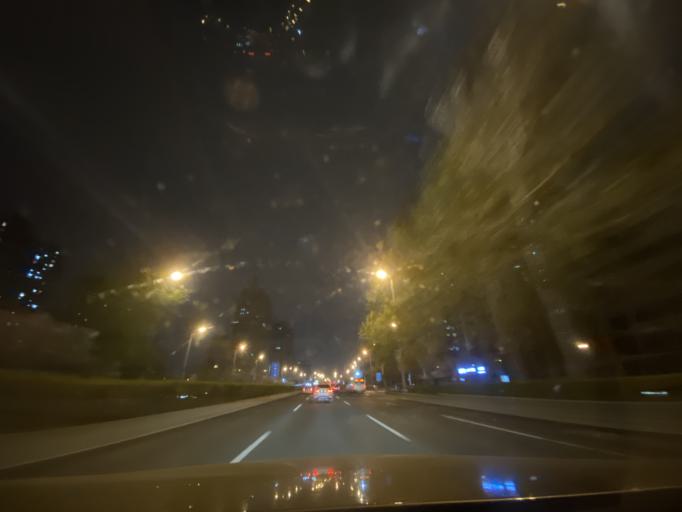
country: CN
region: Beijing
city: Baizhifang
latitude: 39.8959
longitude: 116.3268
